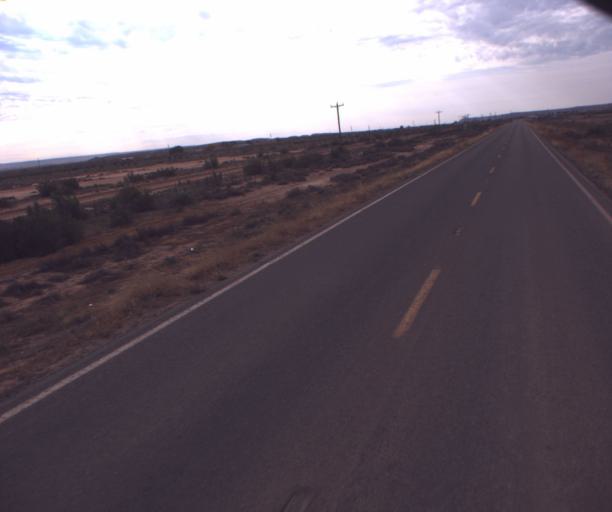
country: US
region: Arizona
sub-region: Apache County
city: Many Farms
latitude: 36.3731
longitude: -109.6128
